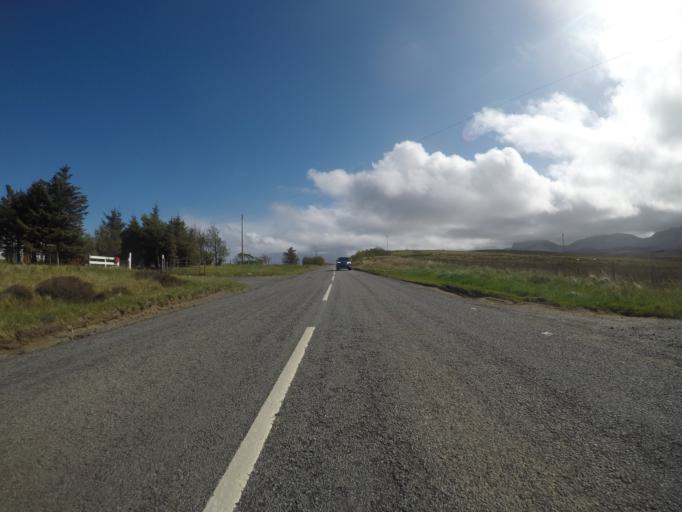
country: GB
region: Scotland
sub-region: Highland
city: Portree
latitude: 57.5780
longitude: -6.1569
